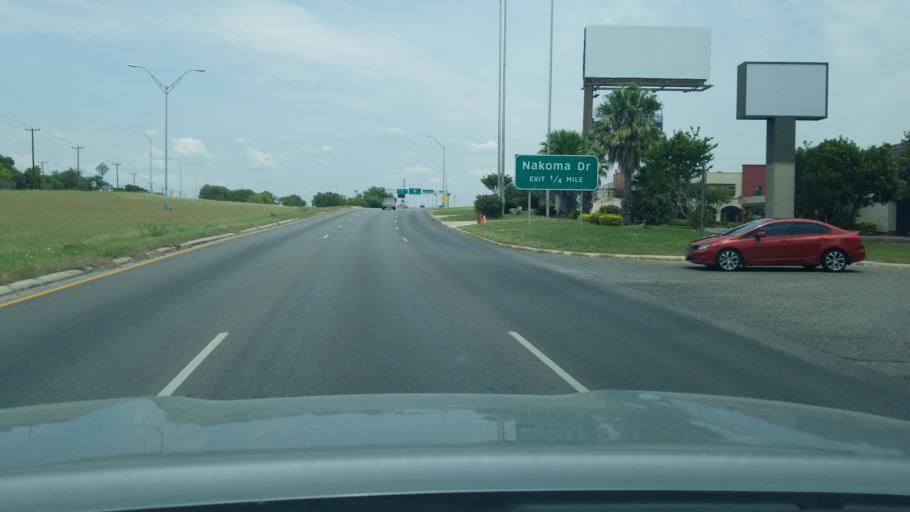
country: US
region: Texas
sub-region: Bexar County
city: Castle Hills
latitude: 29.5341
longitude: -98.4946
